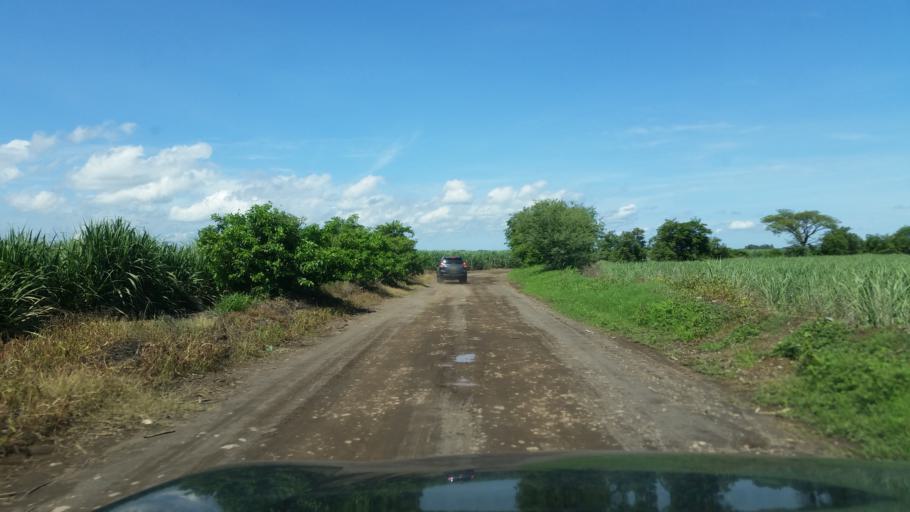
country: NI
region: Chinandega
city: Puerto Morazan
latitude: 12.7738
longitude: -87.1072
